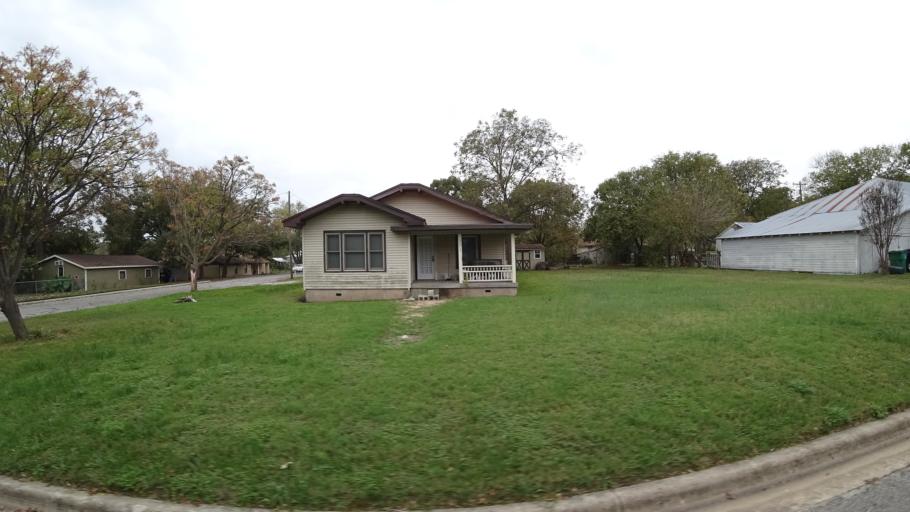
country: US
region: Texas
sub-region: Travis County
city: Pflugerville
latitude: 30.4432
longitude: -97.6213
